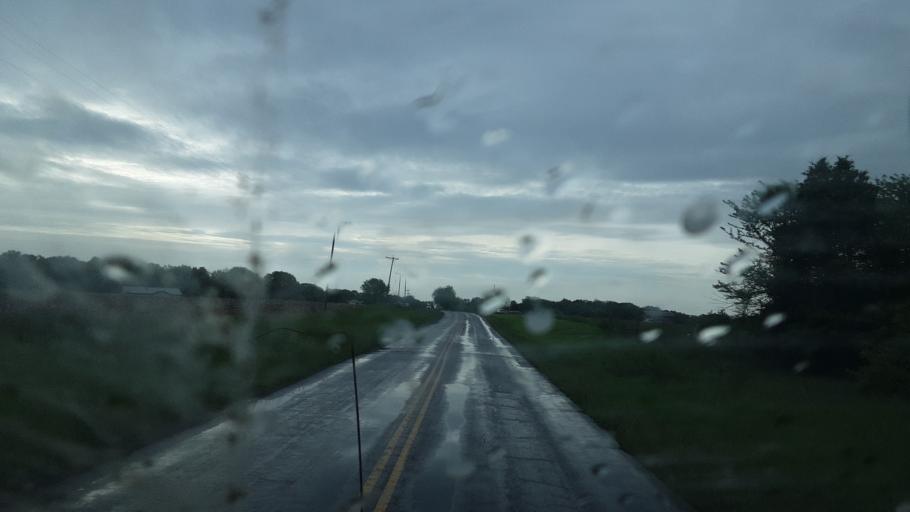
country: US
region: Missouri
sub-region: Clark County
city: Kahoka
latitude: 40.4397
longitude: -91.6011
